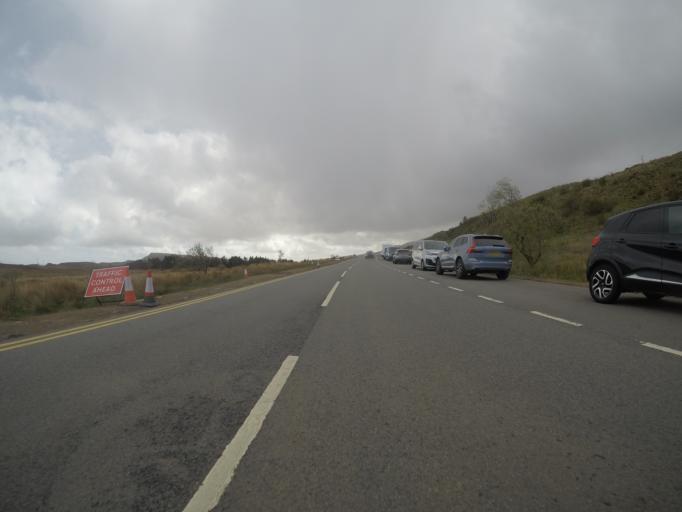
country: GB
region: Scotland
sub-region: Highland
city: Portree
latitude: 57.4983
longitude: -6.1582
